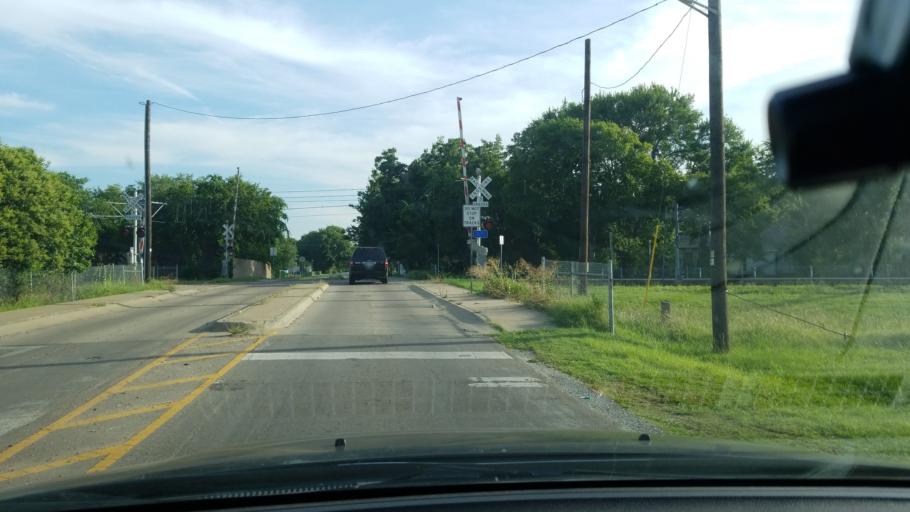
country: US
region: Texas
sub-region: Dallas County
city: Balch Springs
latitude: 32.7202
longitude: -96.6884
